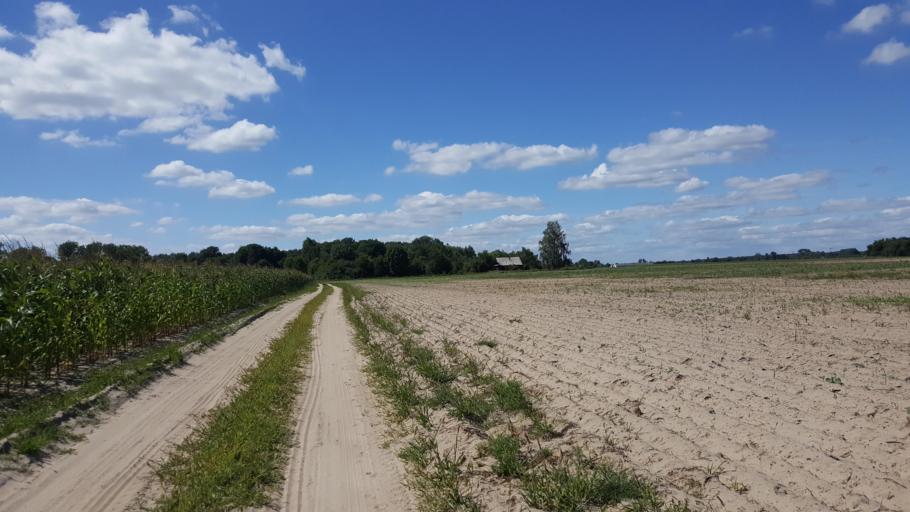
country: BY
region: Brest
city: Kobryn
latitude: 52.3057
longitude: 24.3181
